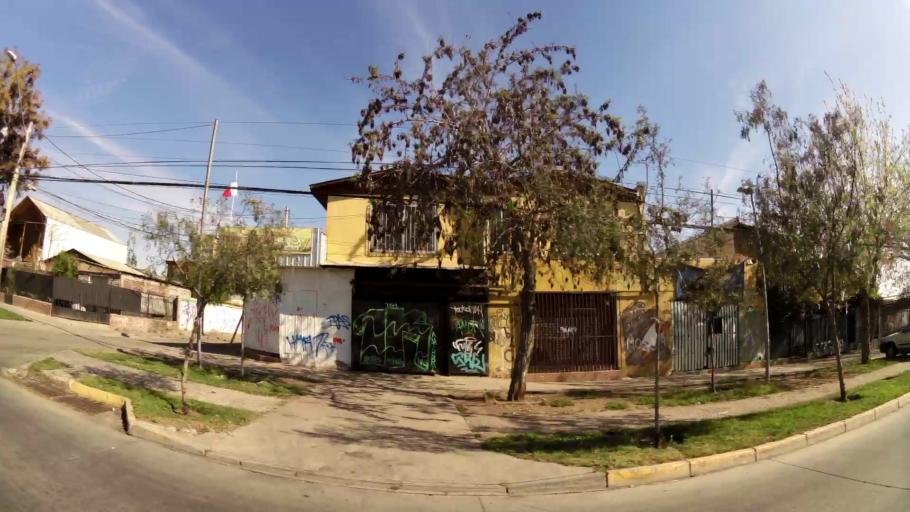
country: CL
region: Santiago Metropolitan
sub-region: Provincia de Santiago
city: Villa Presidente Frei, Nunoa, Santiago, Chile
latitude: -33.4728
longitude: -70.5590
